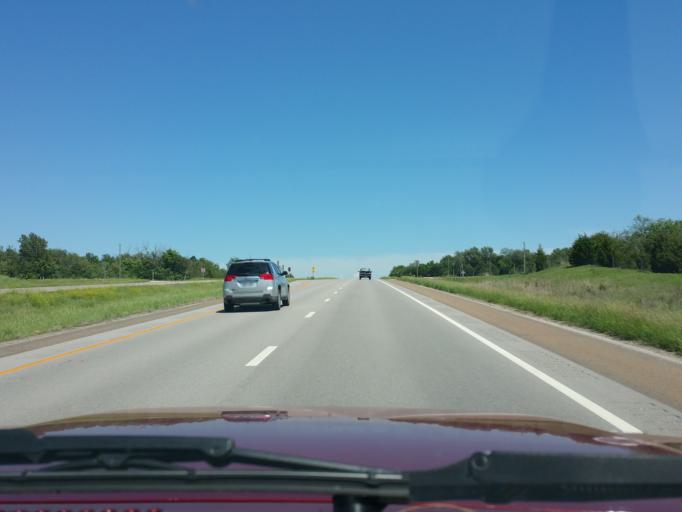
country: US
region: Kansas
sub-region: Pottawatomie County
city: Wamego
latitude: 39.2101
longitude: -96.3538
